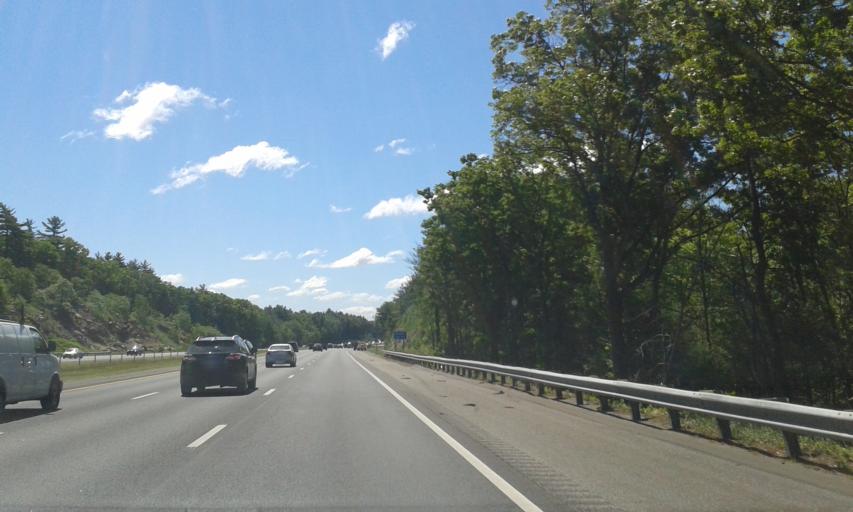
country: US
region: Massachusetts
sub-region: Middlesex County
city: Billerica
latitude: 42.5265
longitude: -71.2694
